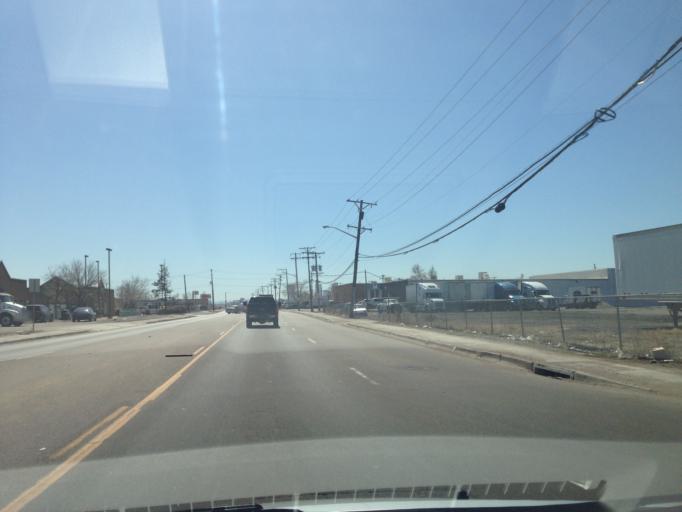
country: US
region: Colorado
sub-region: Adams County
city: Twin Lakes
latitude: 39.8003
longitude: -104.9781
